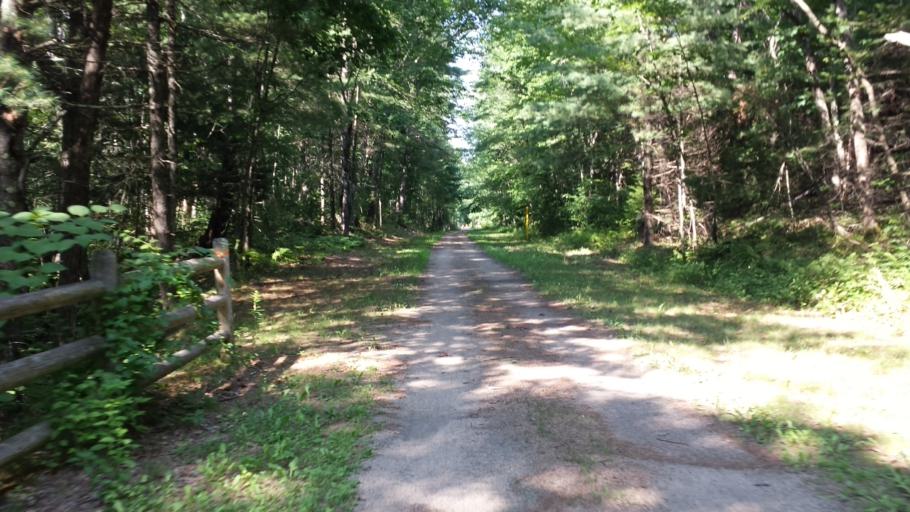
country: US
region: Maine
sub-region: York County
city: Kennebunk
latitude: 43.4450
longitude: -70.5193
